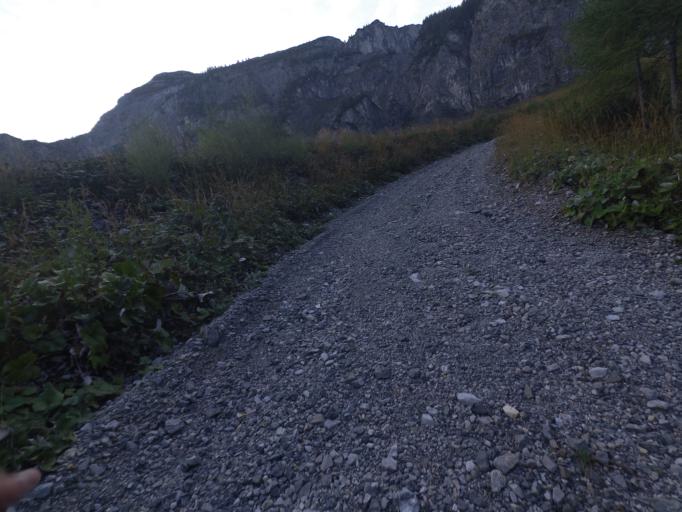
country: AT
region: Salzburg
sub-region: Politischer Bezirk Sankt Johann im Pongau
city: Untertauern
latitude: 47.2352
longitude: 13.4208
